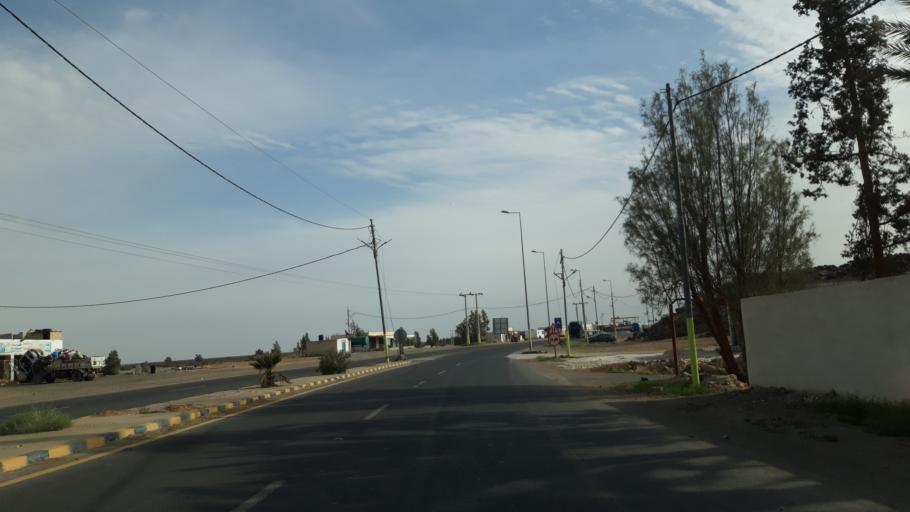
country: JO
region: Amman
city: Al Azraq ash Shamali
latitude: 31.8756
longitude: 36.8256
